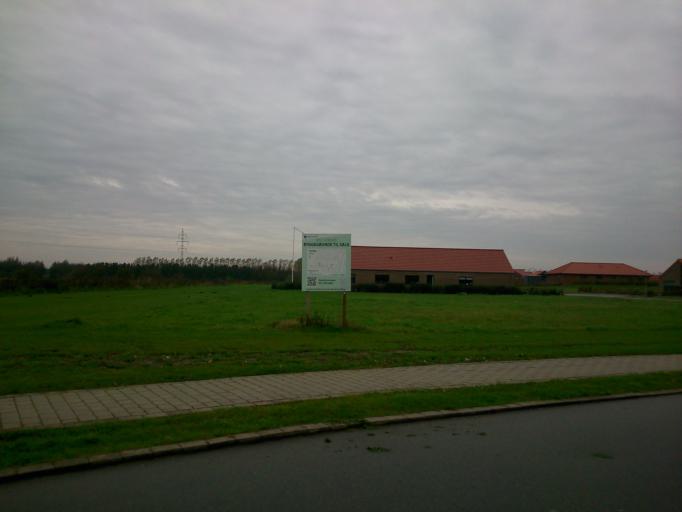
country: DK
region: South Denmark
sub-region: Varde Kommune
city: Varde
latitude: 55.6215
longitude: 8.4588
